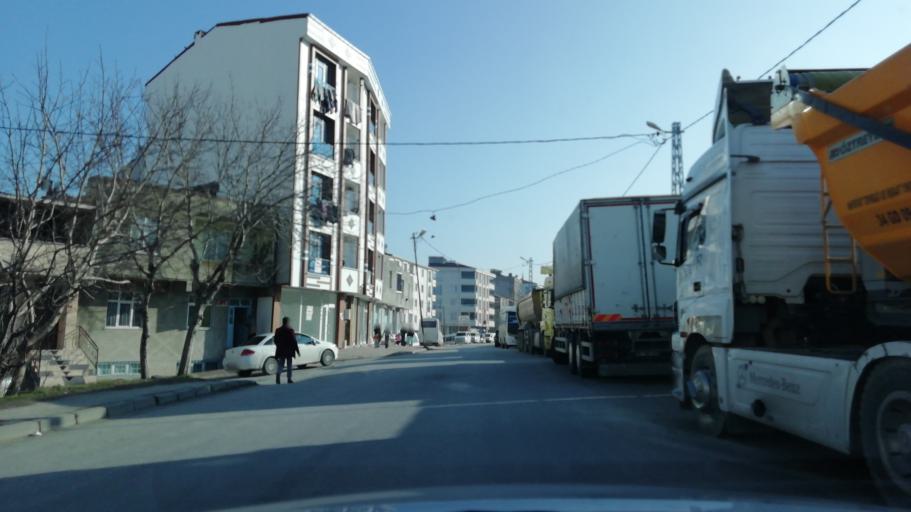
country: TR
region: Istanbul
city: Esenyurt
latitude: 41.0364
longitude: 28.6889
